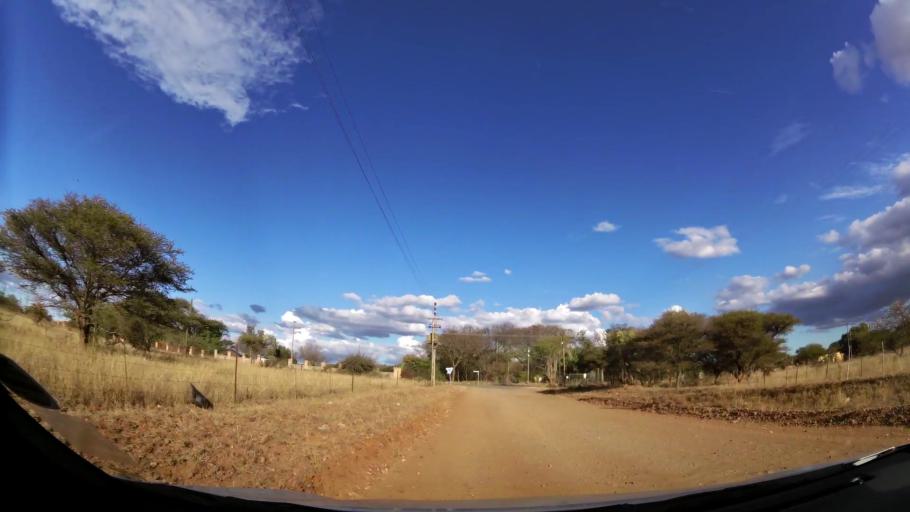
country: ZA
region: Limpopo
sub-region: Capricorn District Municipality
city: Polokwane
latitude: -23.9326
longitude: 29.4367
